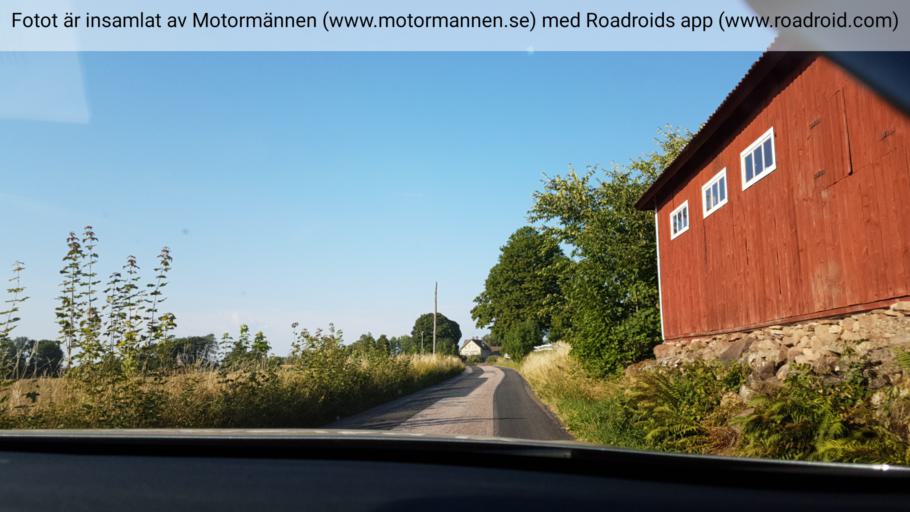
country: SE
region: Vaestra Goetaland
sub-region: Skara Kommun
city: Axvall
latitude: 58.4394
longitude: 13.6969
